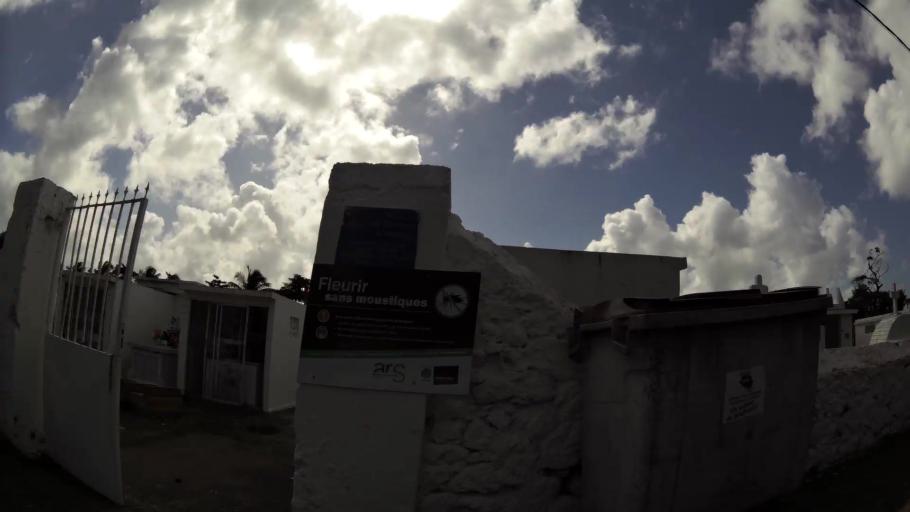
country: MQ
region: Martinique
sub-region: Martinique
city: Les Trois-Ilets
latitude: 14.4792
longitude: -61.0285
